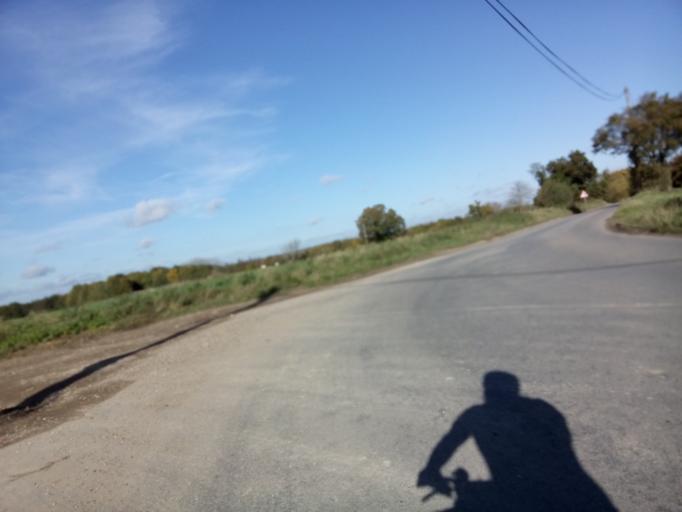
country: GB
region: England
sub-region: Suffolk
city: Bramford
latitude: 52.0263
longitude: 1.0976
